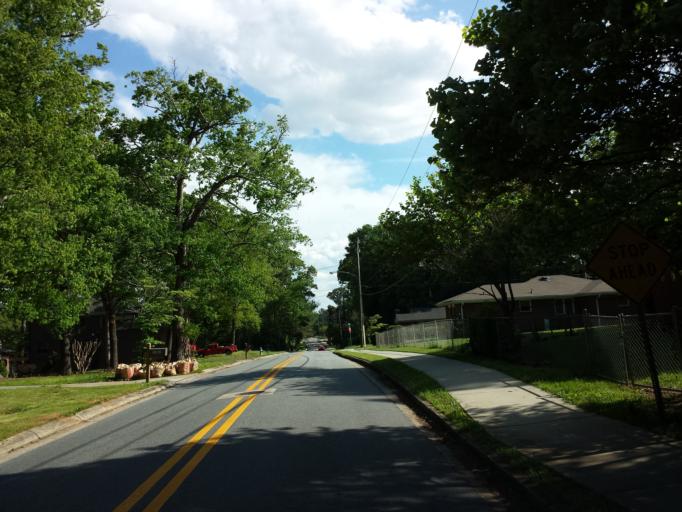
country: US
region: Georgia
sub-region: Cobb County
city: Smyrna
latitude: 33.8711
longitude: -84.5187
